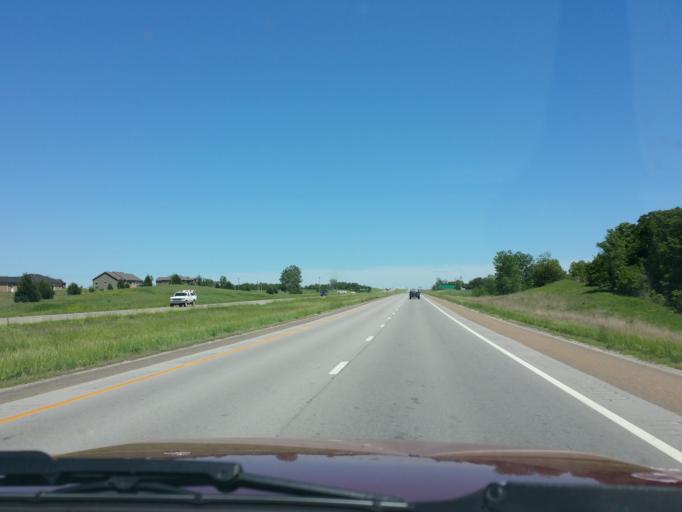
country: US
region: Kansas
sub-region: Pottawatomie County
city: Wamego
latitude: 39.2096
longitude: -96.4034
